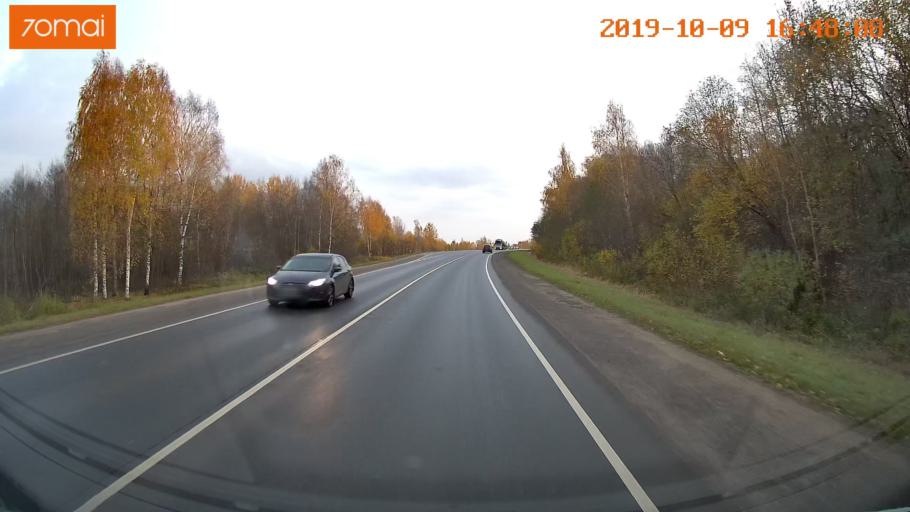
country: RU
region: Kostroma
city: Volgorechensk
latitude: 57.4311
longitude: 41.1888
